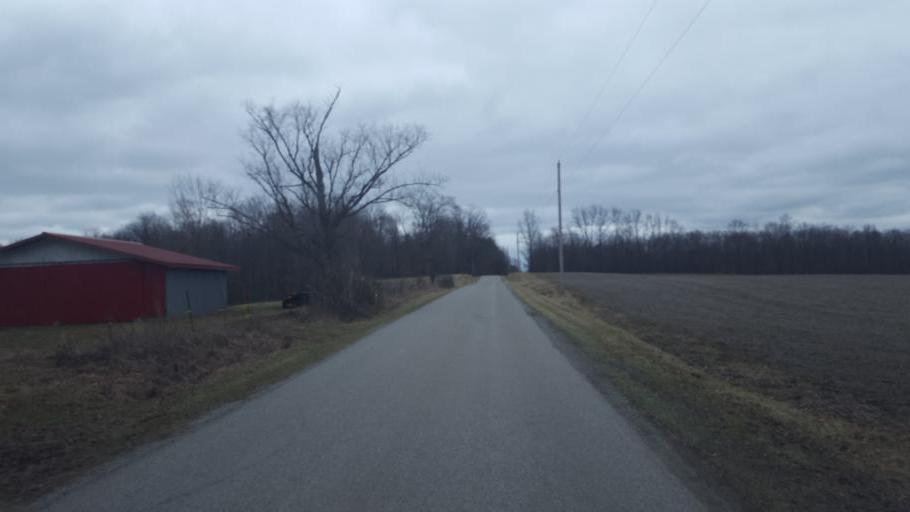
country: US
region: Ohio
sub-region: Crawford County
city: Galion
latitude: 40.6644
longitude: -82.7020
